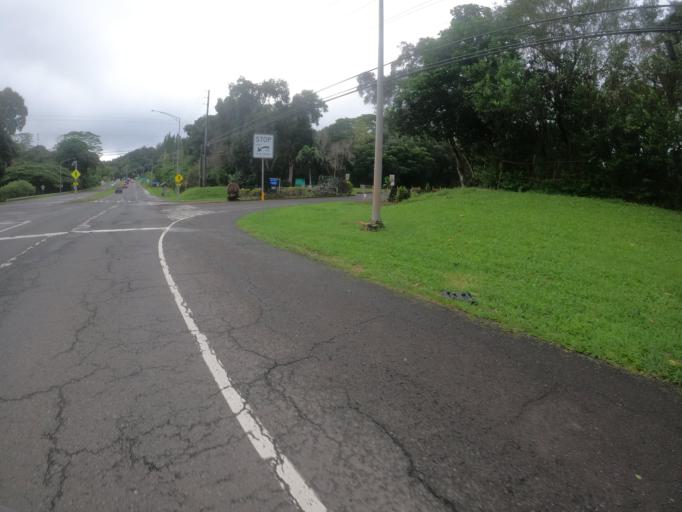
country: US
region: Hawaii
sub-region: Honolulu County
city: Maunawili
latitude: 21.3771
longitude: -157.7832
